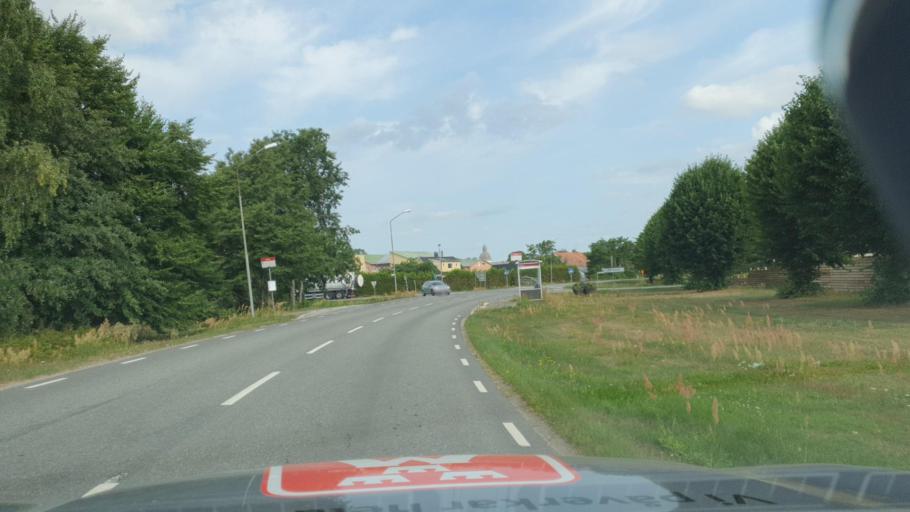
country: SE
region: Blekinge
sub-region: Solvesborgs Kommun
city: Soelvesborg
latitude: 56.0460
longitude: 14.6841
